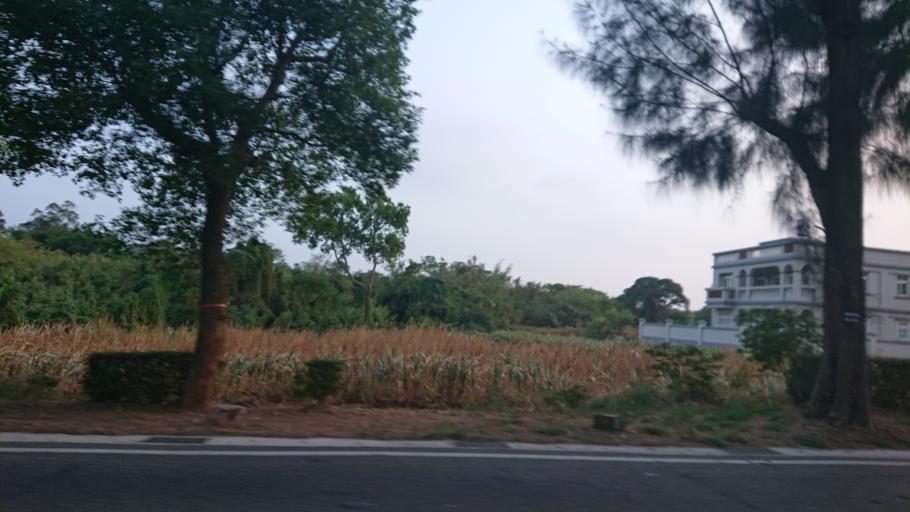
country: TW
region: Fukien
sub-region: Kinmen
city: Jincheng
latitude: 24.4521
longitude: 118.3504
